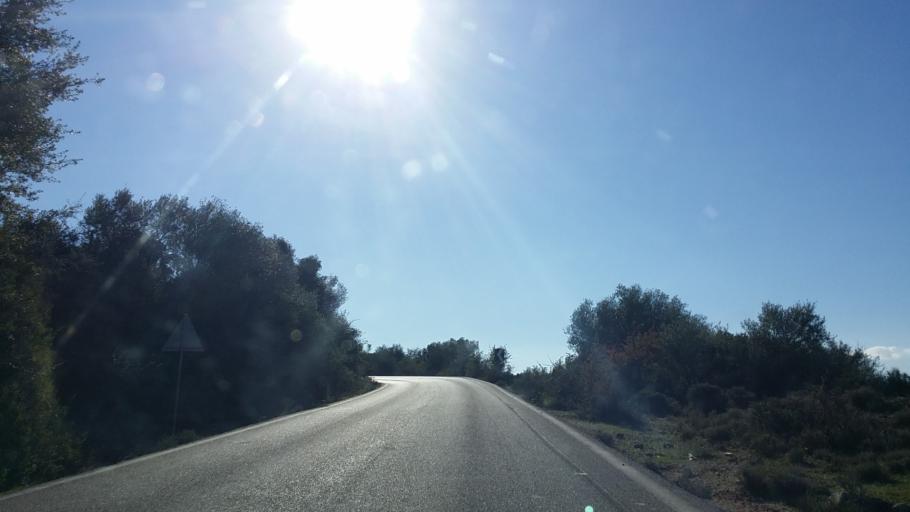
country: GR
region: West Greece
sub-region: Nomos Aitolias kai Akarnanias
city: Palairos
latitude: 38.7363
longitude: 20.8953
